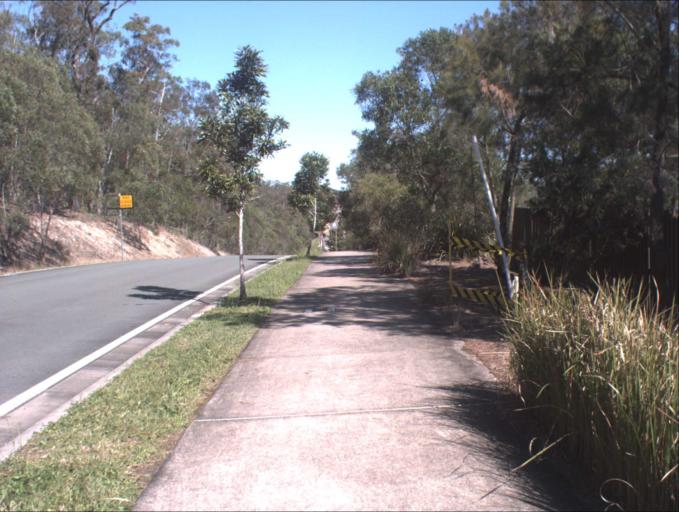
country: AU
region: Queensland
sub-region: Logan
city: Windaroo
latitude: -27.7232
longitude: 153.1734
